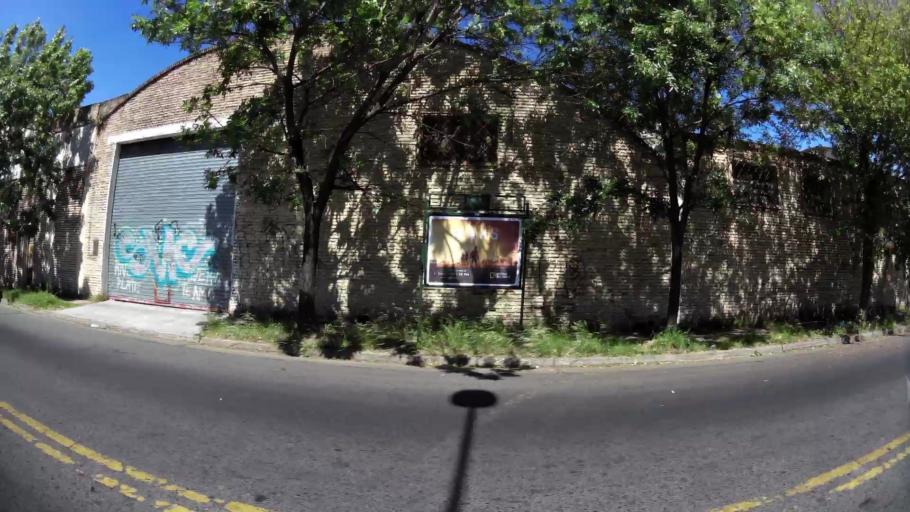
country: AR
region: Buenos Aires
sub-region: Partido de General San Martin
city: General San Martin
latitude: -34.5398
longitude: -58.5388
